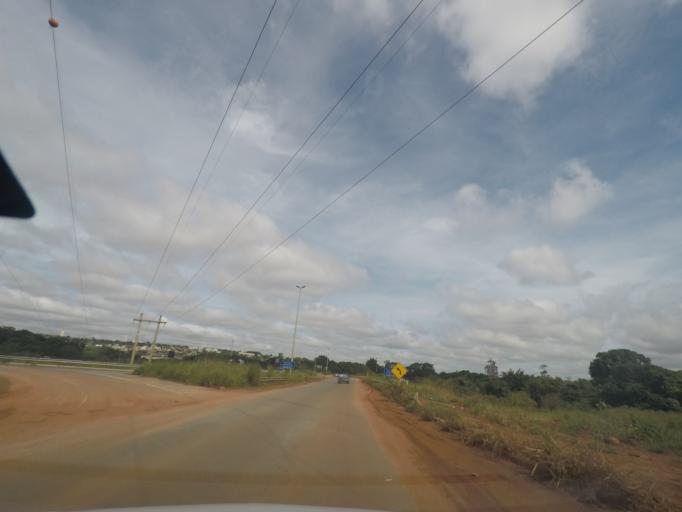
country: BR
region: Goias
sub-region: Goiania
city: Goiania
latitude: -16.6753
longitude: -49.1958
